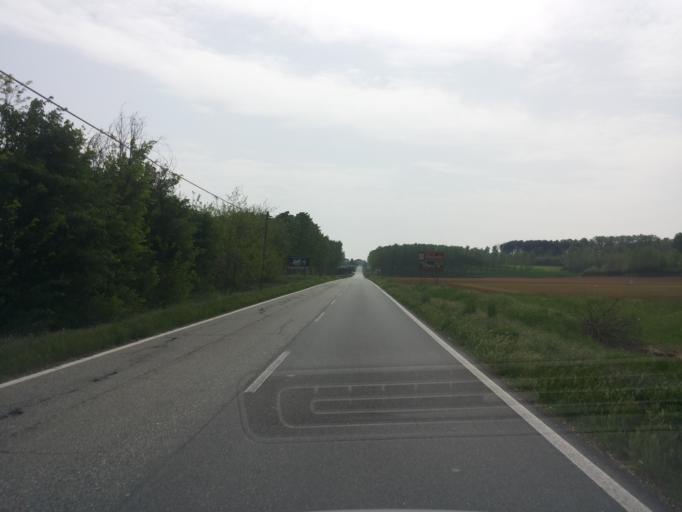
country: IT
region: Piedmont
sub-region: Provincia di Alessandria
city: Mirabello Monferrato
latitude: 45.0464
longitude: 8.5194
